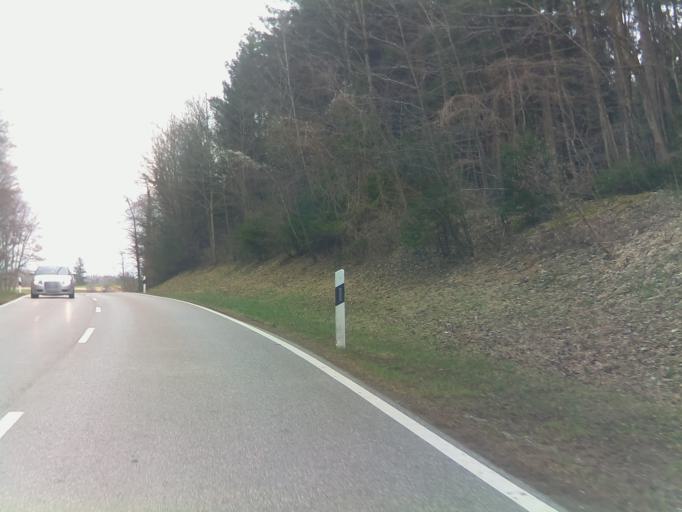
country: DE
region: Bavaria
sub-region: Upper Bavaria
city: Weilheim
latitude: 47.8174
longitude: 11.2215
